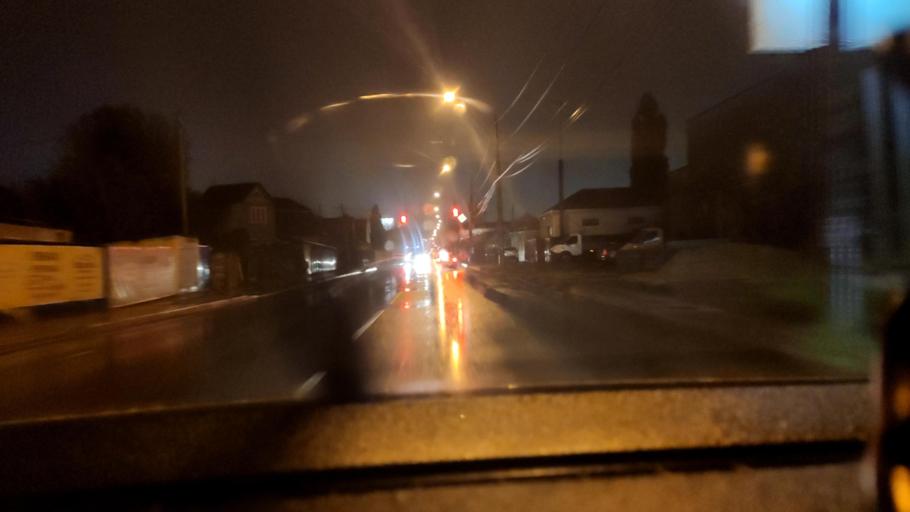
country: RU
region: Voronezj
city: Voronezh
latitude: 51.6890
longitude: 39.2099
